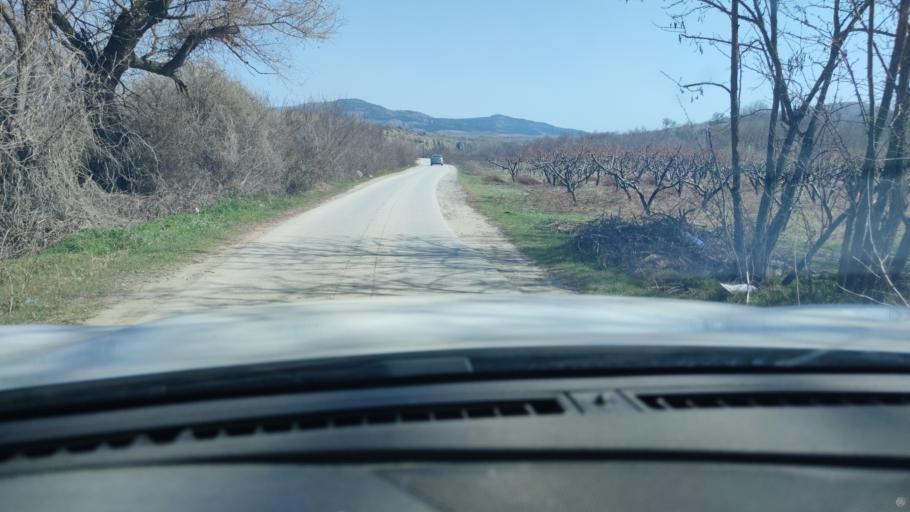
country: MK
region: Rosoman
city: Rosoman
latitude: 41.4732
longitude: 21.9140
